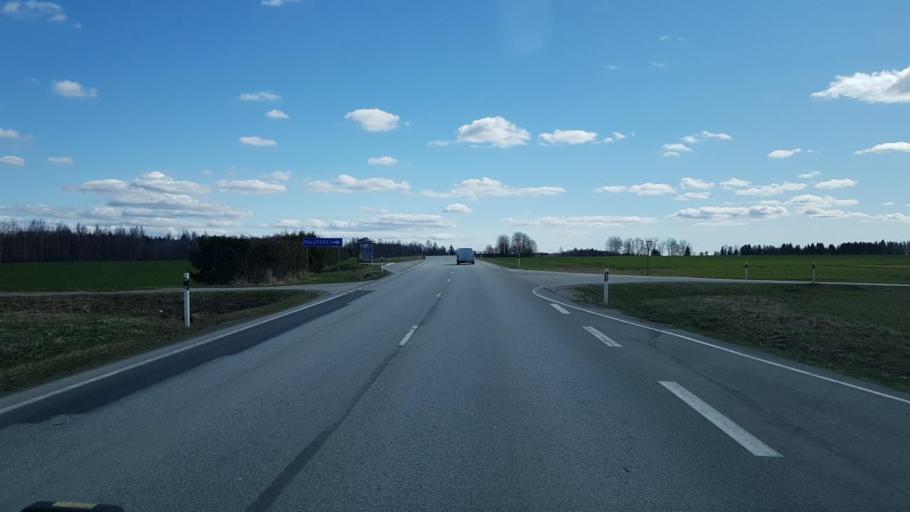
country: EE
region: Jogevamaa
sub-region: Jogeva linn
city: Jogeva
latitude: 58.8161
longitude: 26.5570
